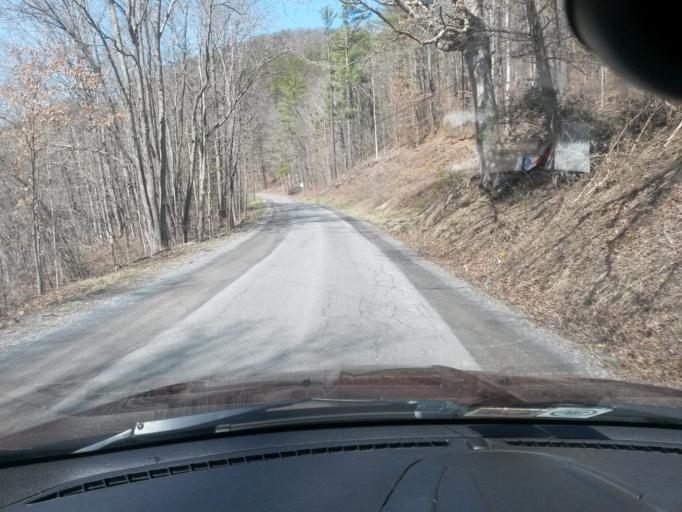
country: US
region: West Virginia
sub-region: Greenbrier County
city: White Sulphur Springs
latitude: 37.7734
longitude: -80.2814
